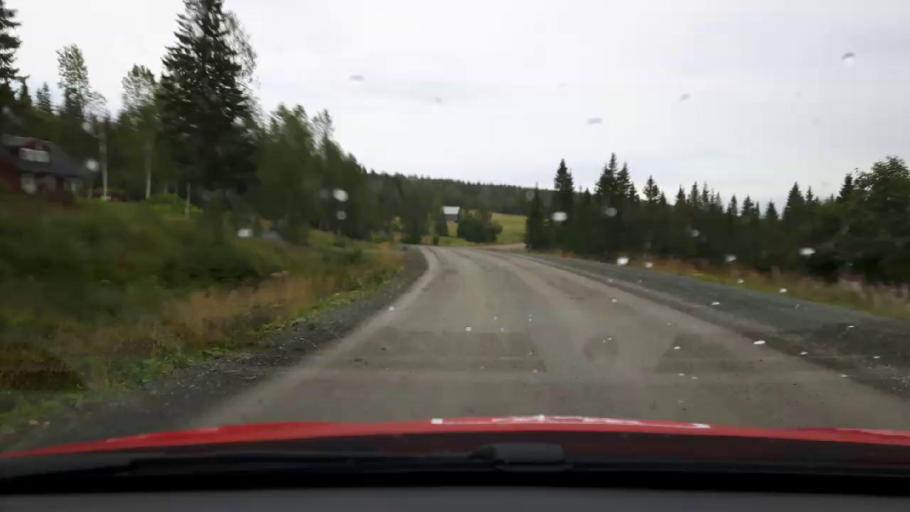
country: SE
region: Jaemtland
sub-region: Are Kommun
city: Are
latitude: 63.4633
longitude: 12.6267
